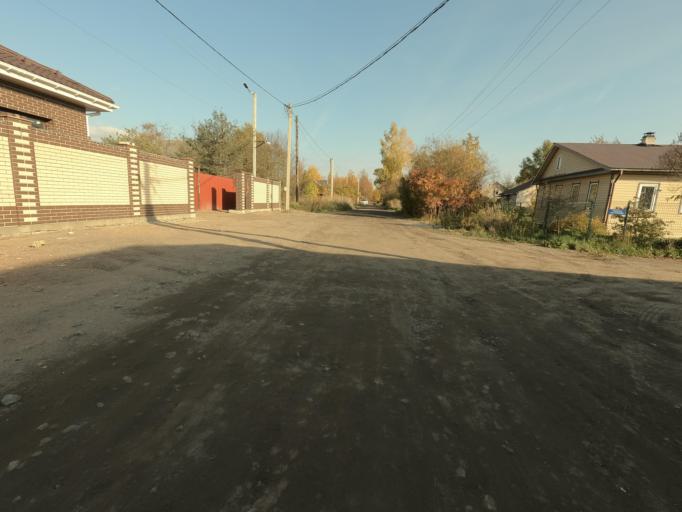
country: RU
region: Leningrad
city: Mga
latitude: 59.7525
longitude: 31.0647
